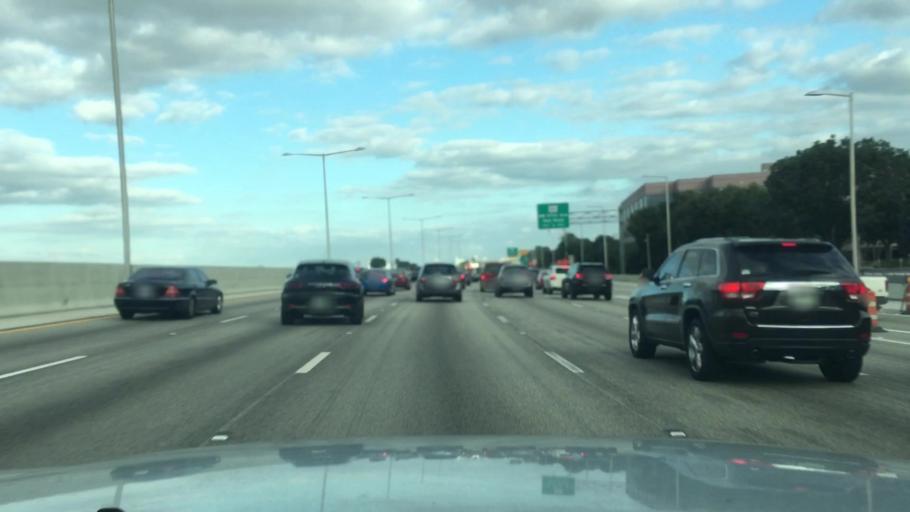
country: US
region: Florida
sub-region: Miami-Dade County
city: West Miami
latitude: 25.7840
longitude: -80.3024
